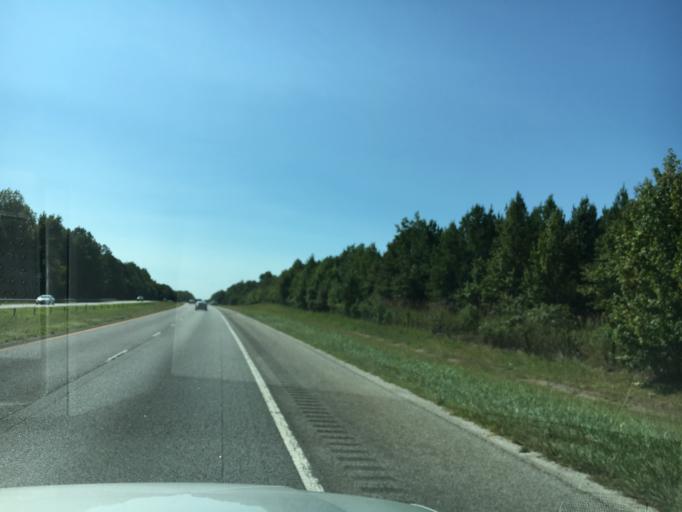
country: US
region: South Carolina
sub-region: Spartanburg County
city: Roebuck
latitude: 34.8029
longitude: -81.9605
